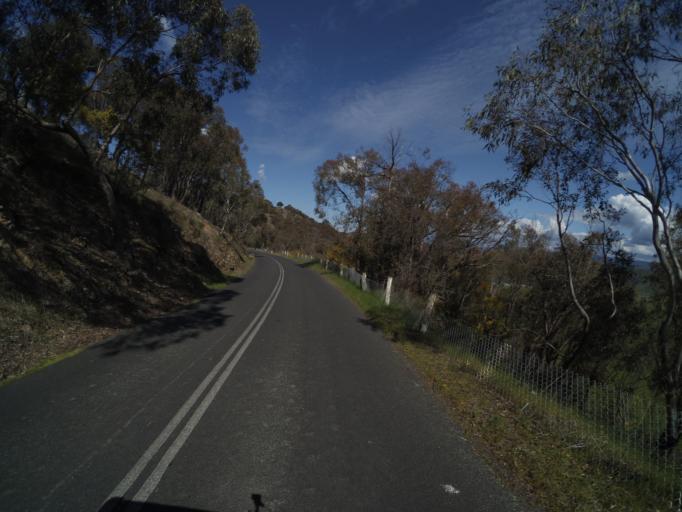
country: AU
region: New South Wales
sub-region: Yass Valley
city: Yass
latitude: -34.9900
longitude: 148.8412
